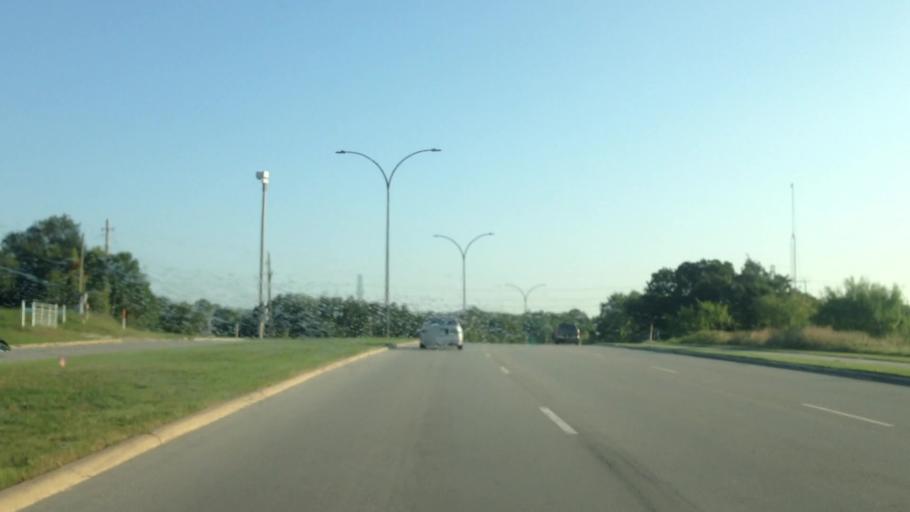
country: US
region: Texas
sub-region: Tarrant County
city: Pantego
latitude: 32.7200
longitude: -97.1829
